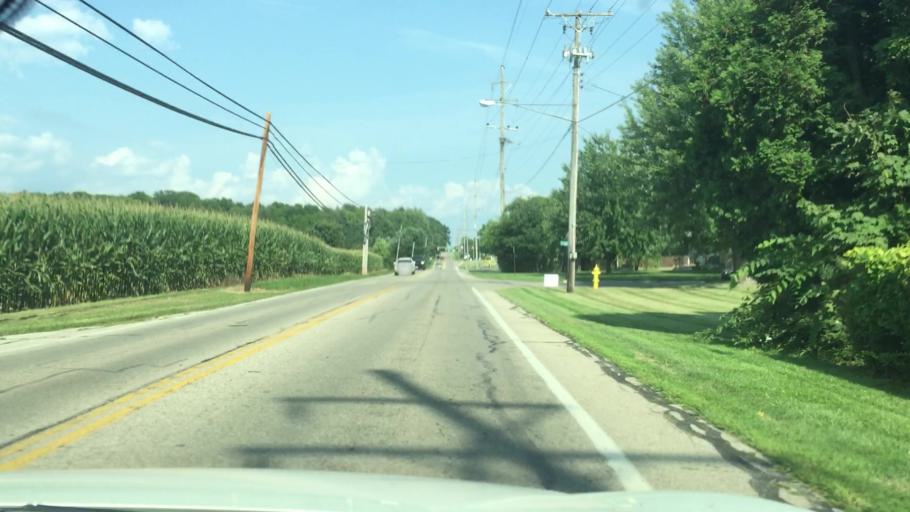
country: US
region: Ohio
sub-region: Clark County
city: Northridge
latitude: 39.9951
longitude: -83.7674
